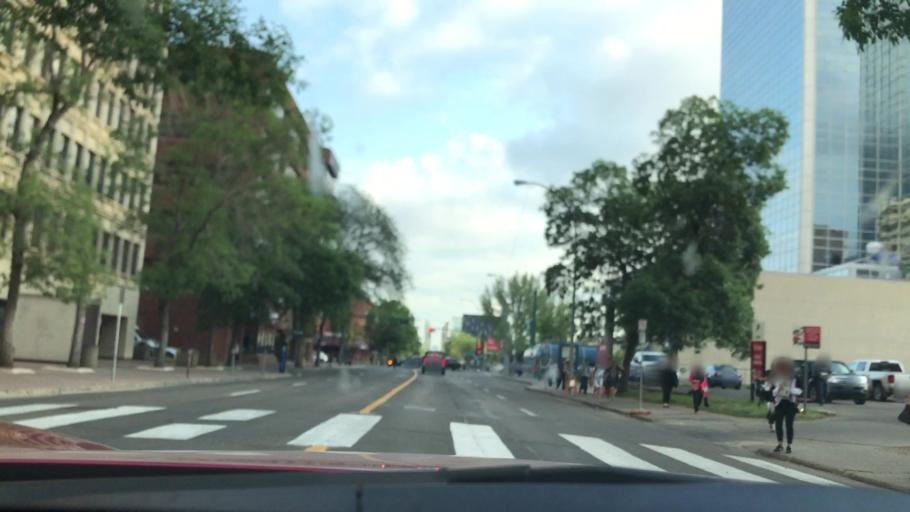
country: CA
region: Alberta
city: Edmonton
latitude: 53.5397
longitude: -113.5048
